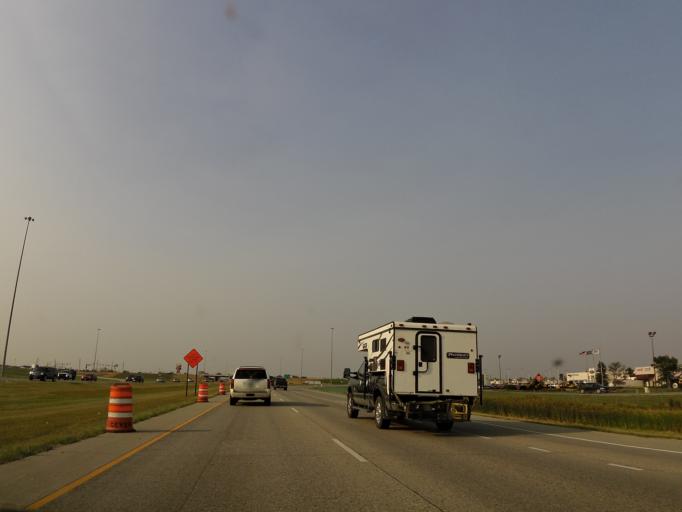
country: US
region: North Dakota
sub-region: Cass County
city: Fargo
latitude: 46.8276
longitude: -96.8397
